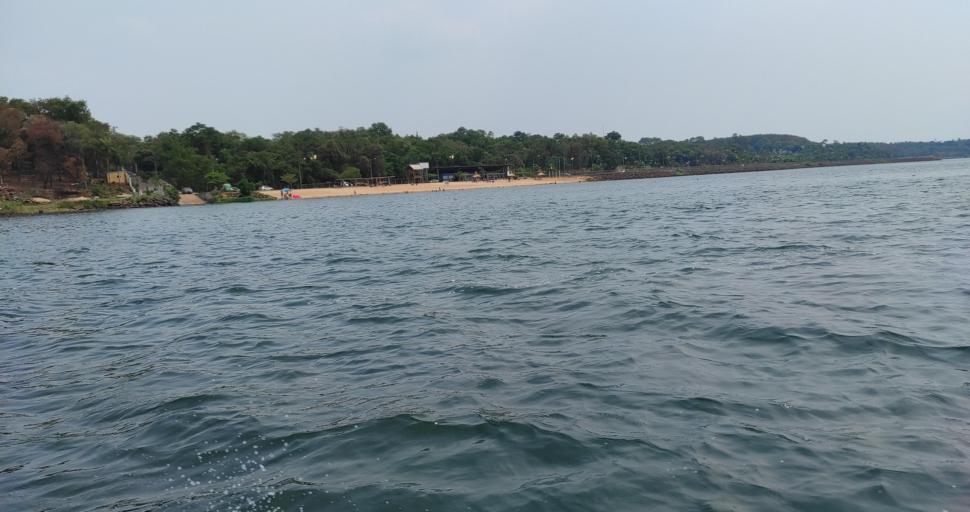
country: AR
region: Misiones
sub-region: Departamento de Candelaria
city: Candelaria
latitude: -27.4468
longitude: -55.7481
